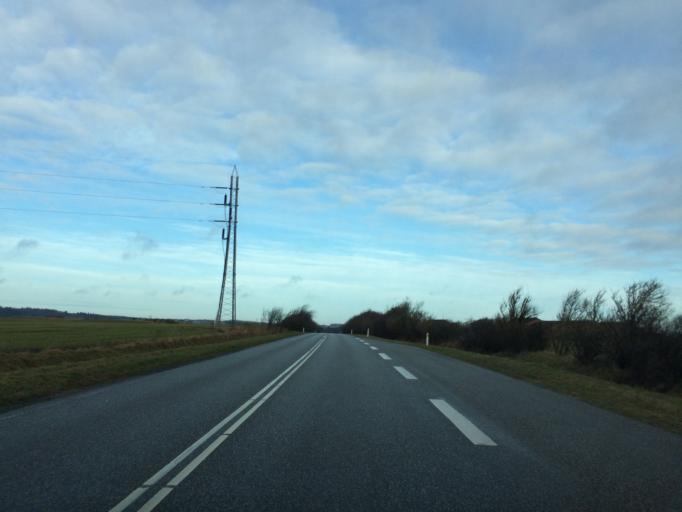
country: DK
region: Central Jutland
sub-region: Struer Kommune
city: Struer
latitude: 56.4798
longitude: 8.5539
